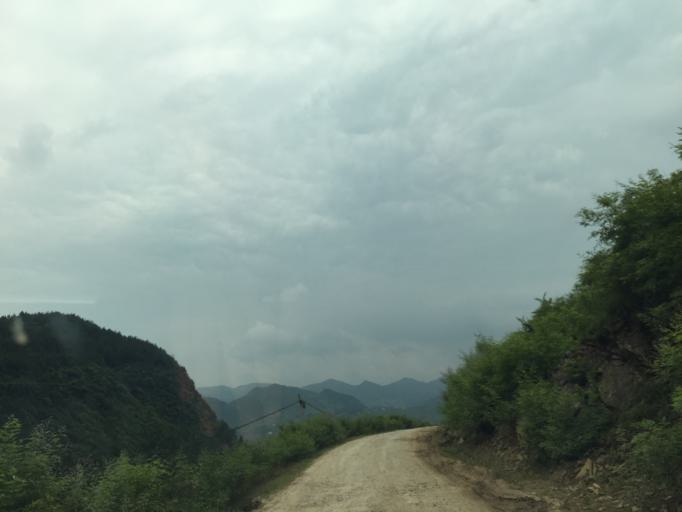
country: CN
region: Guizhou Sheng
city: Tongjing
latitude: 28.3661
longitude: 108.2350
